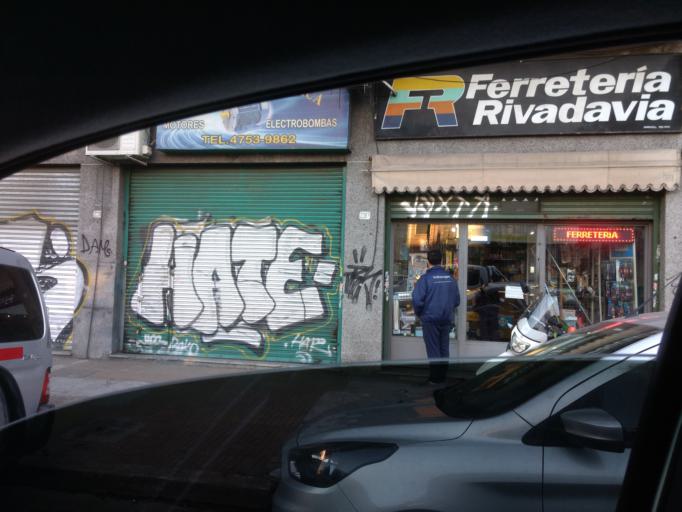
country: AR
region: Buenos Aires
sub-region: Partido de General San Martin
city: General San Martin
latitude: -34.5779
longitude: -58.5454
